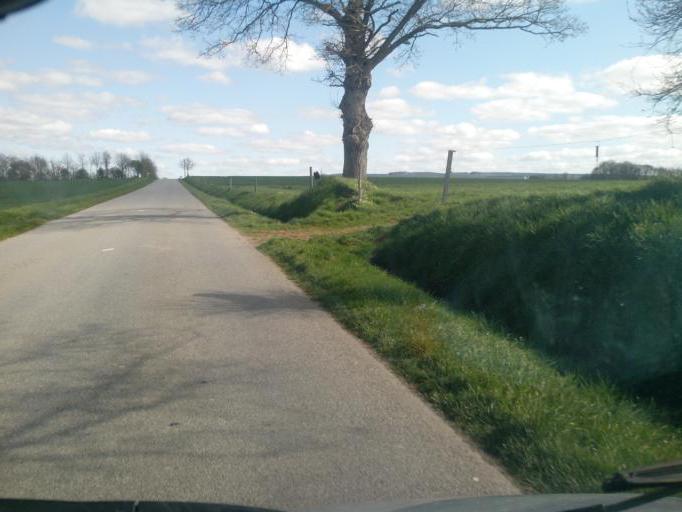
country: FR
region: Brittany
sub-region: Departement du Morbihan
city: Mauron
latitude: 48.0807
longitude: -2.2671
